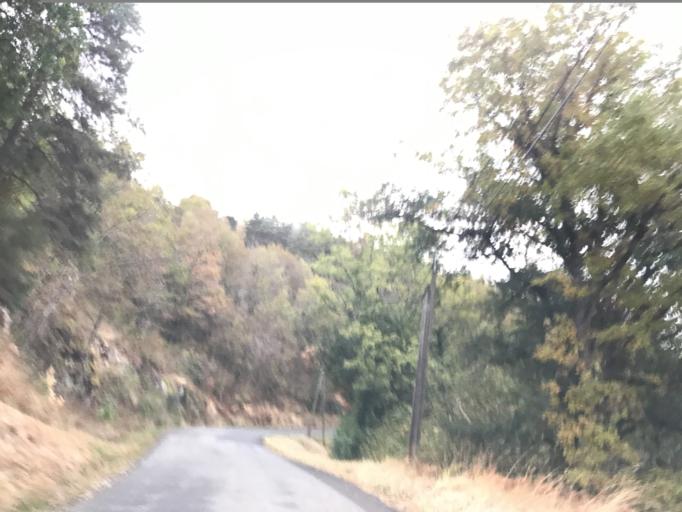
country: FR
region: Auvergne
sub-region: Departement du Puy-de-Dome
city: Escoutoux
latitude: 45.8289
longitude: 3.5660
